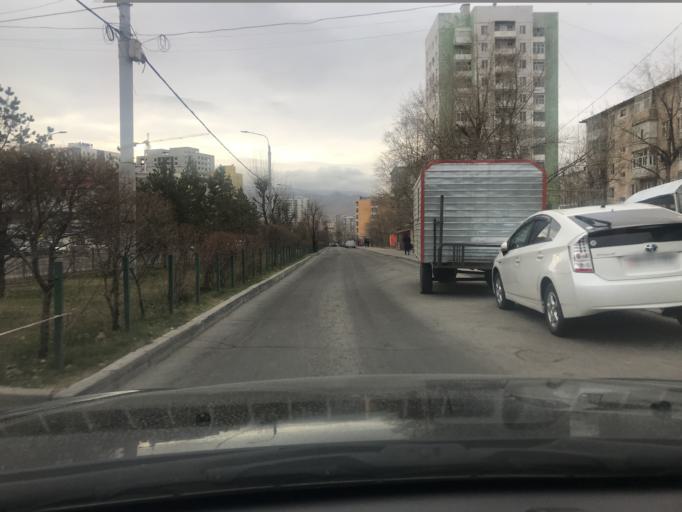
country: MN
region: Ulaanbaatar
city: Ulaanbaatar
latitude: 47.9223
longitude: 106.9422
